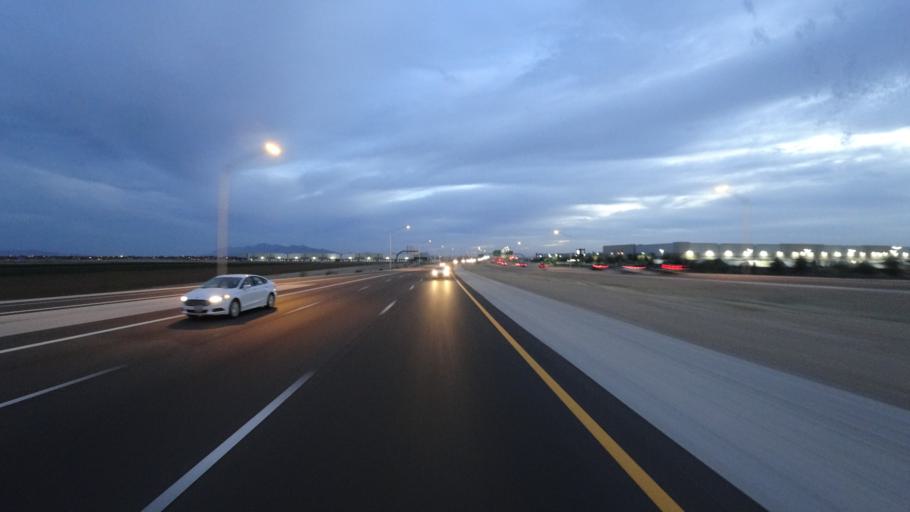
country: US
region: Arizona
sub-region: Maricopa County
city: Citrus Park
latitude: 33.5048
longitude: -112.4185
